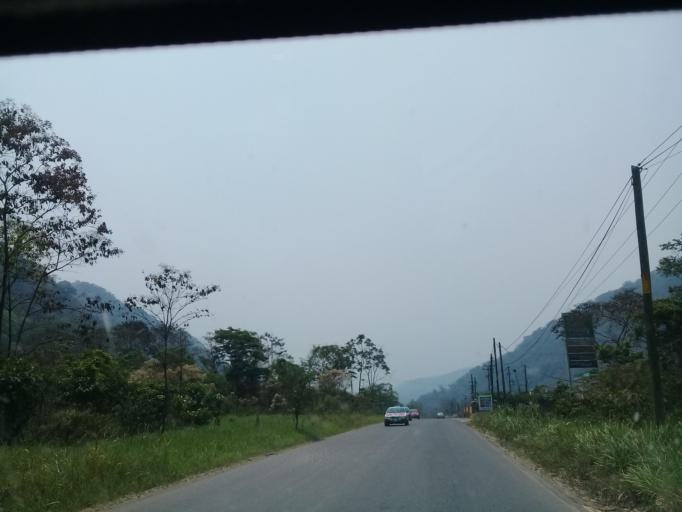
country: MX
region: Veracruz
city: Tezonapa
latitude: 18.6194
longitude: -96.6993
